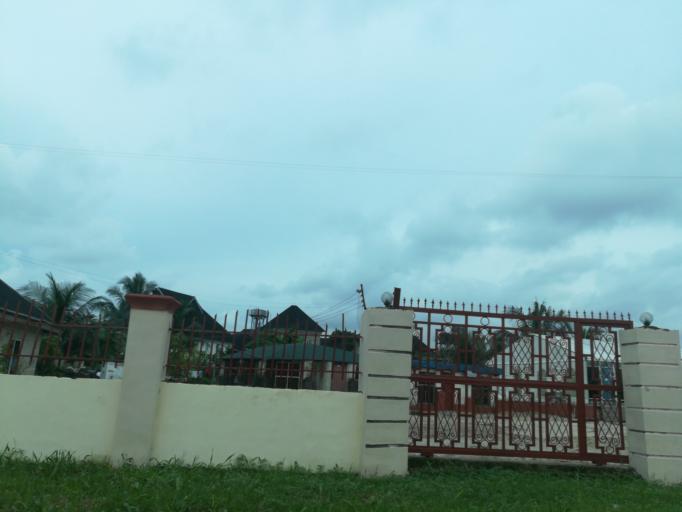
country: NG
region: Rivers
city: Port Harcourt
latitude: 4.8185
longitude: 6.9888
